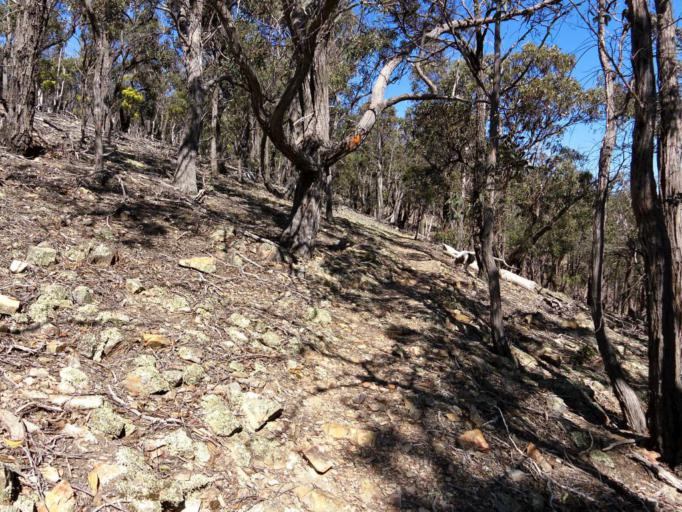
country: AU
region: Victoria
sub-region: Moorabool
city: Bacchus Marsh
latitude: -37.6673
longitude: 144.3210
